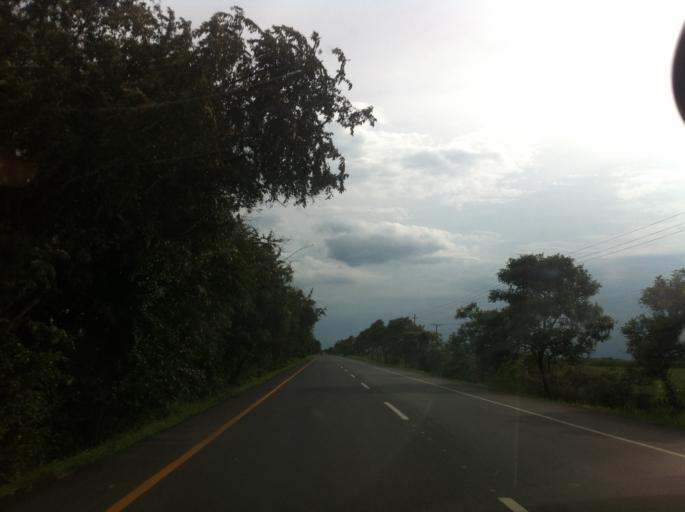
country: CO
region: Valle del Cauca
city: Palmira
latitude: 3.5587
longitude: -76.3357
